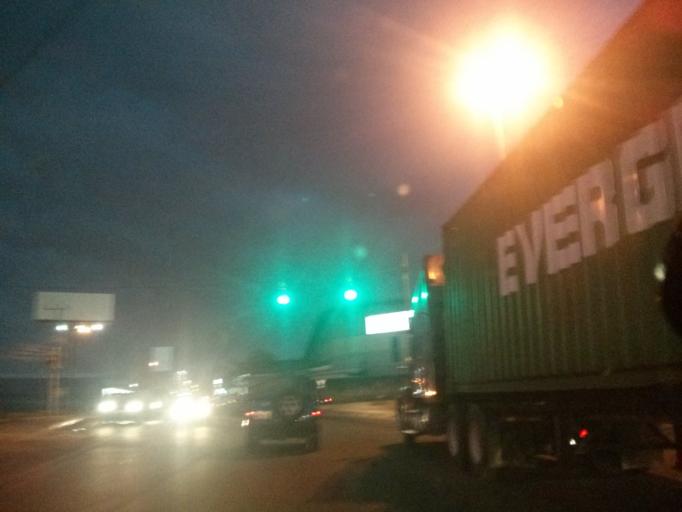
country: CR
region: San Jose
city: Colima
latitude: 9.9506
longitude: -84.1031
